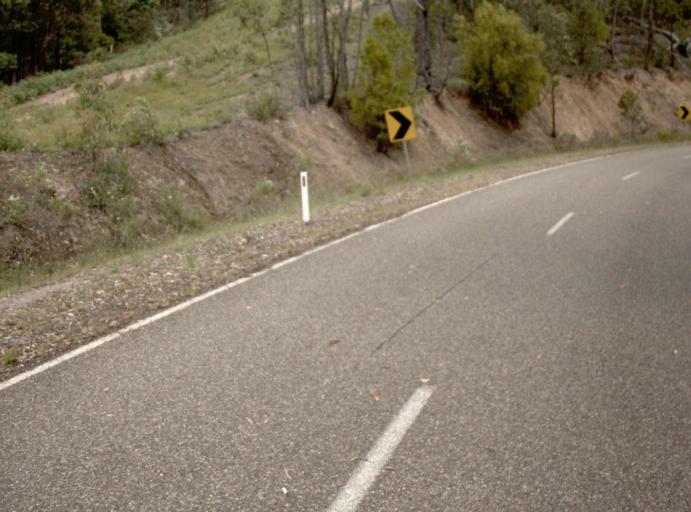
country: AU
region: Victoria
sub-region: East Gippsland
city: Bairnsdale
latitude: -37.6626
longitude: 147.2796
